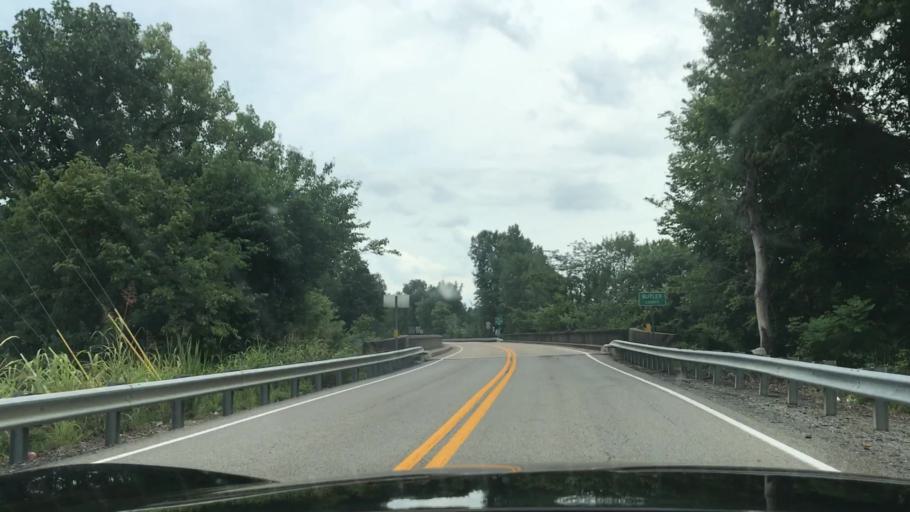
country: US
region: Kentucky
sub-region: Ohio County
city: Beaver Dam
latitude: 37.2110
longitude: -86.9007
